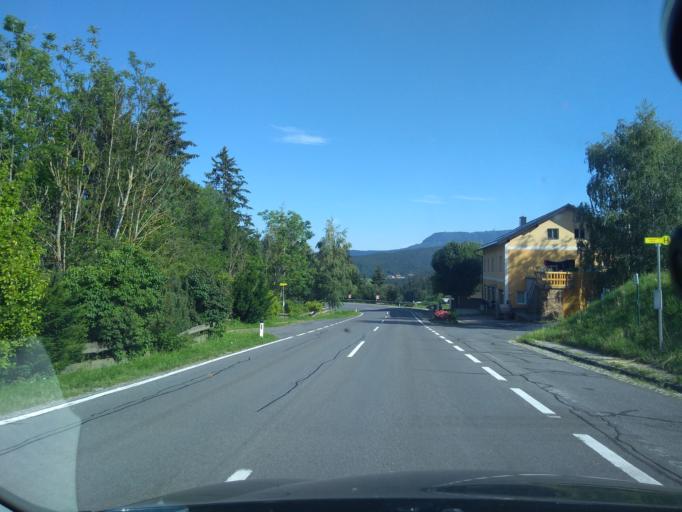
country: AT
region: Styria
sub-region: Politischer Bezirk Graz-Umgebung
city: Semriach
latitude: 47.2681
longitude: 15.4240
